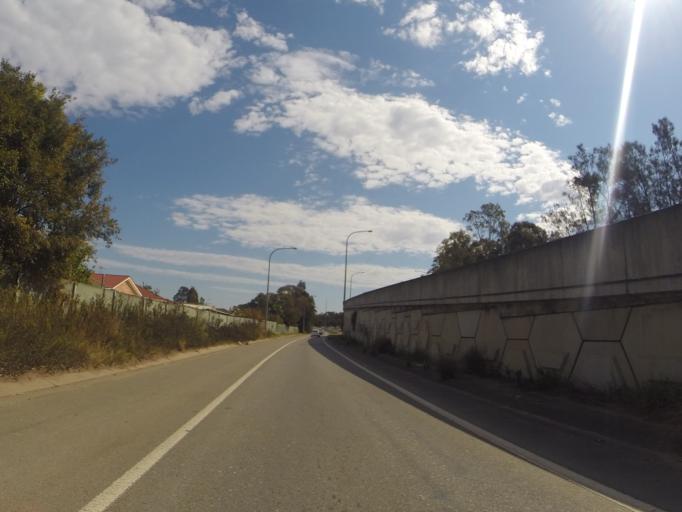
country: AU
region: New South Wales
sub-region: Bankstown
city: Milperra
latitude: -33.9435
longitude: 150.9441
